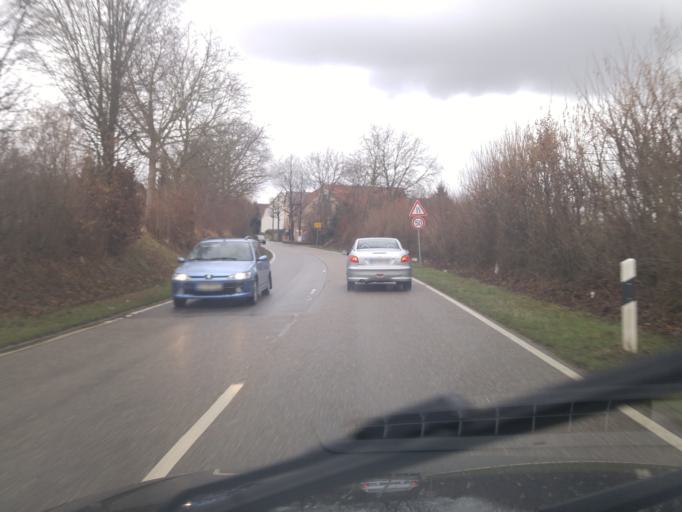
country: DE
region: Baden-Wuerttemberg
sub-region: Regierungsbezirk Stuttgart
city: Affalterbach
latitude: 48.9261
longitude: 9.3207
